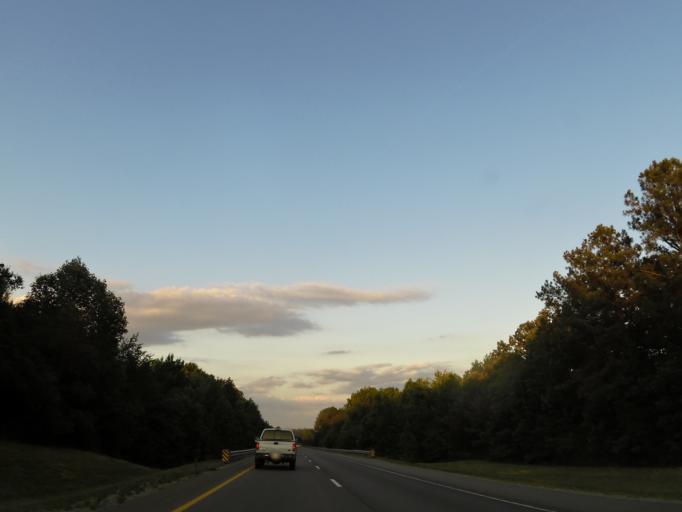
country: US
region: Tennessee
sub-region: Putnam County
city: Baxter
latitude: 36.1400
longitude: -85.5917
